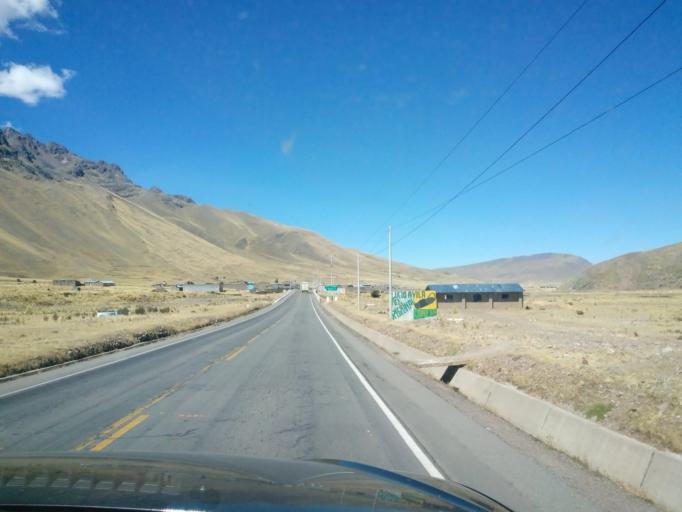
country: PE
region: Puno
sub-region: Provincia de Melgar
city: Santa Rosa
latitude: -14.5336
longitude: -70.8883
